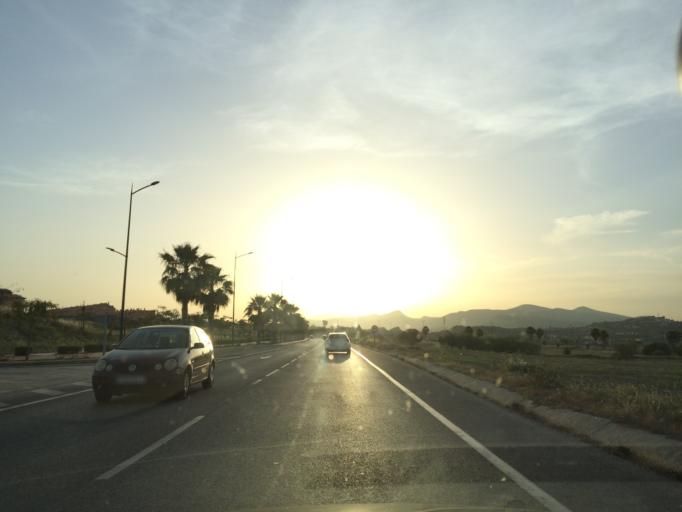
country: ES
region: Andalusia
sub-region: Provincia de Malaga
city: Alhaurin de la Torre
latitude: 36.6697
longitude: -4.5509
